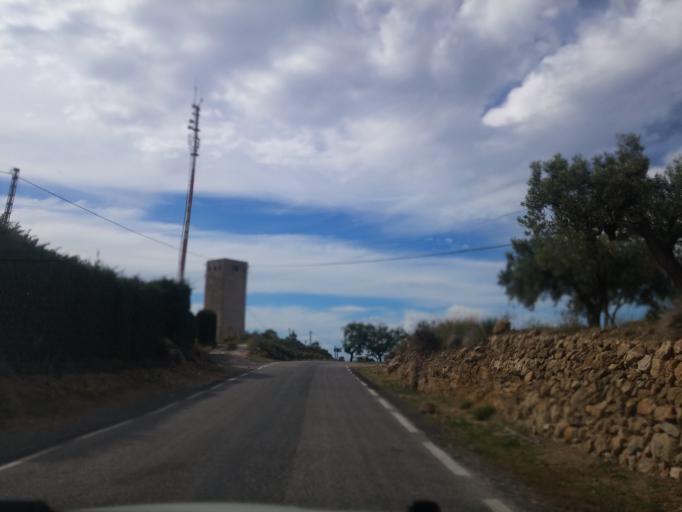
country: ES
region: Valencia
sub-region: Provincia de Alicante
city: Benissa
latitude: 38.7054
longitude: 0.0180
